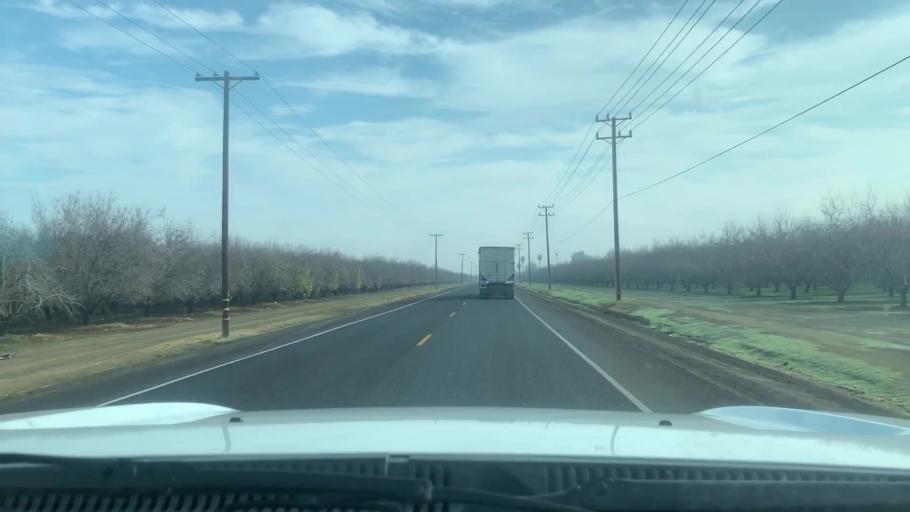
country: US
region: California
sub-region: Kern County
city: Lost Hills
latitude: 35.4992
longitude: -119.6784
